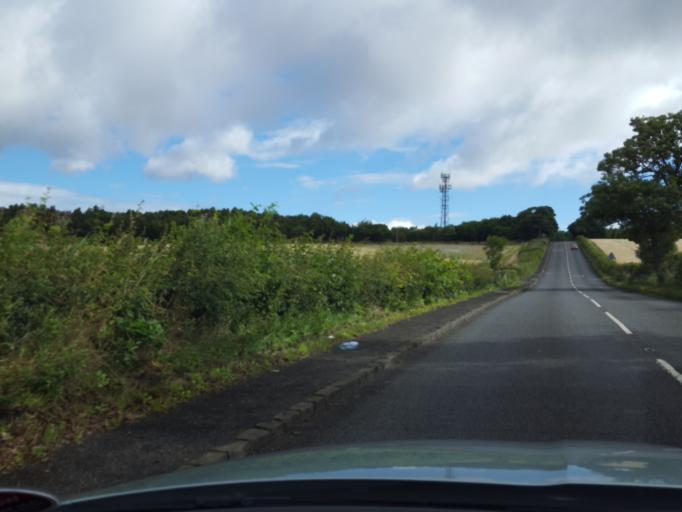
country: GB
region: Scotland
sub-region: West Lothian
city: Linlithgow
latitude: 55.9941
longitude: -3.6121
